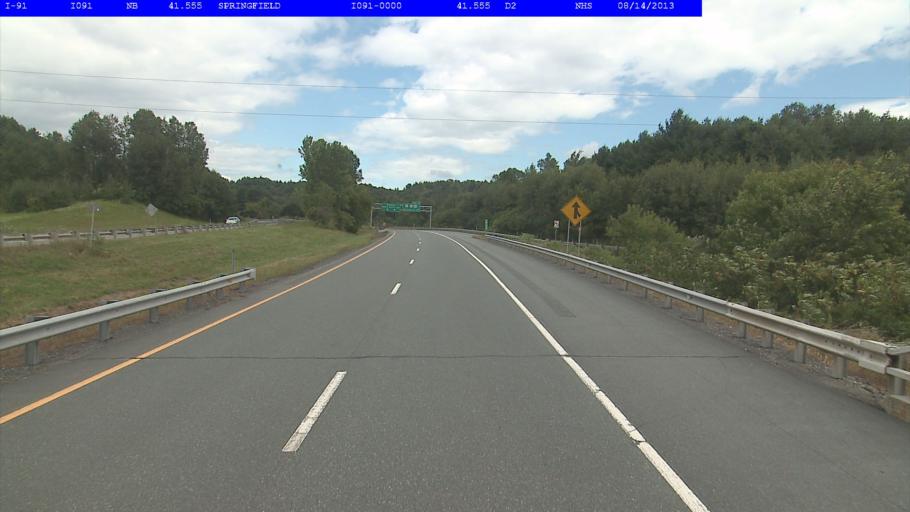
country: US
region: New Hampshire
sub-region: Sullivan County
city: Charlestown
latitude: 43.2649
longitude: -72.4332
